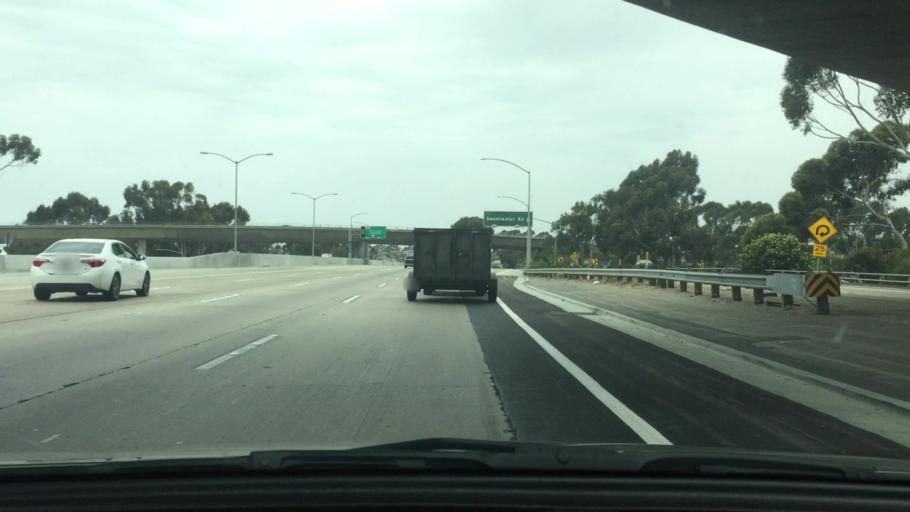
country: US
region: California
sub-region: San Diego County
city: Chula Vista
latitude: 32.6575
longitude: -117.0735
